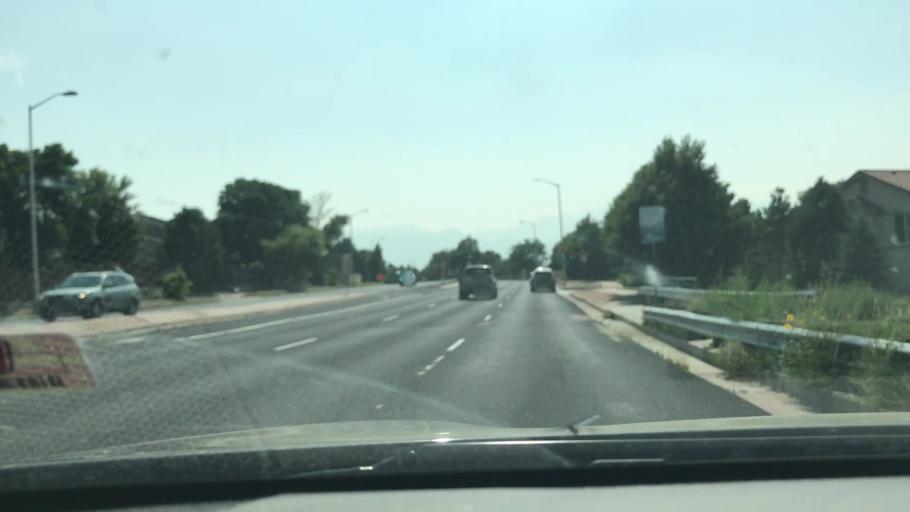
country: US
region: Colorado
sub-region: El Paso County
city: Black Forest
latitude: 38.9477
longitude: -104.7717
